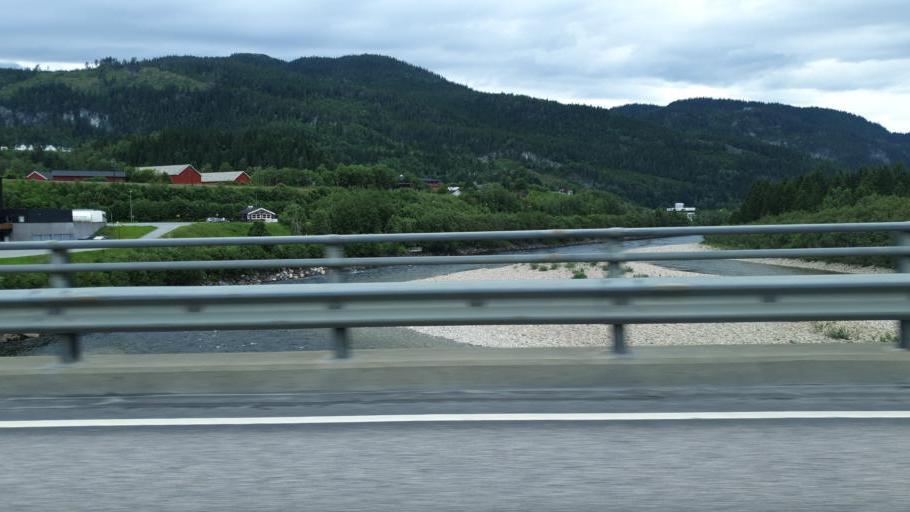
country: NO
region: Sor-Trondelag
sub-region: Midtre Gauldal
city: Storen
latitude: 63.0367
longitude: 10.2959
